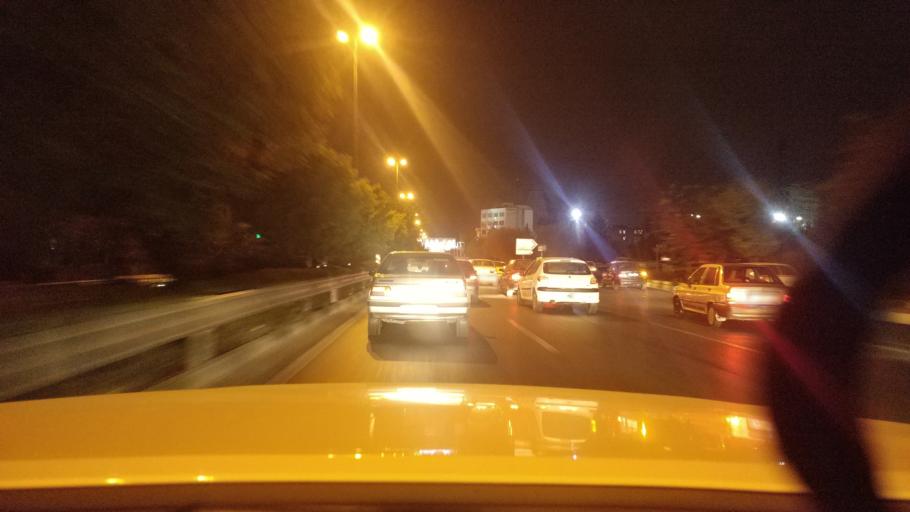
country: IR
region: Tehran
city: Tehran
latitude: 35.7395
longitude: 51.3294
